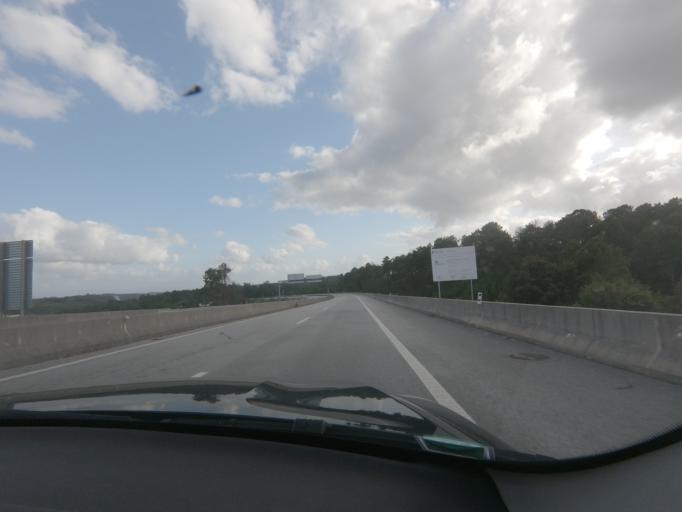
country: PT
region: Viseu
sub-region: Viseu
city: Abraveses
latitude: 40.6676
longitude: -7.9699
